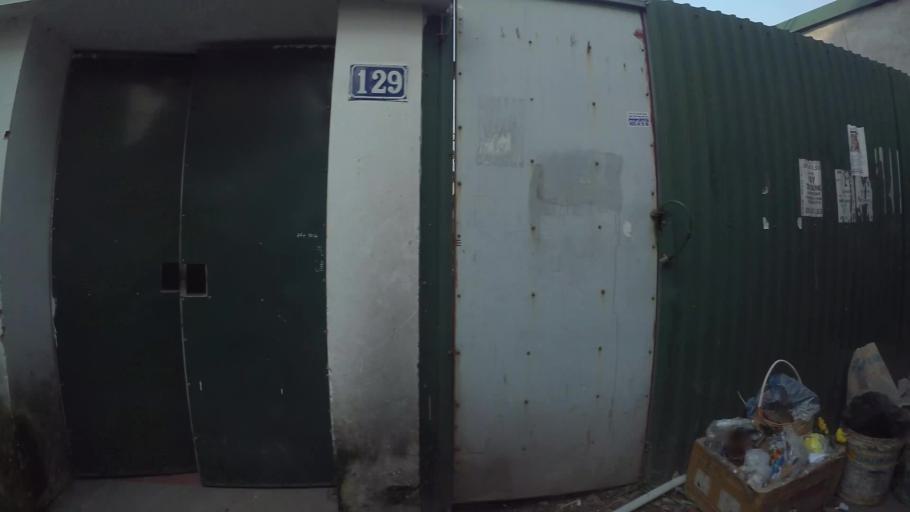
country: VN
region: Ha Noi
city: Thanh Xuan
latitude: 20.9788
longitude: 105.8291
